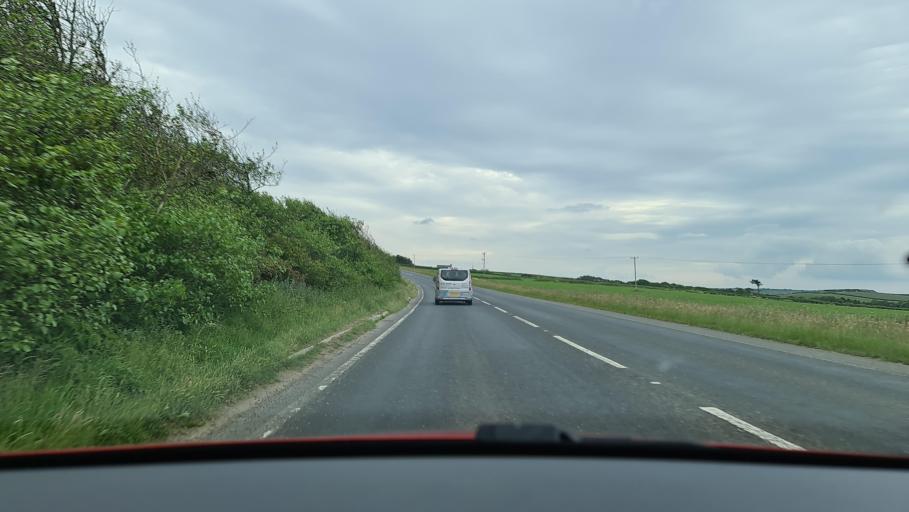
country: GB
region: England
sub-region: Cornwall
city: Poundstock
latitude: 50.7803
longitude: -4.5393
